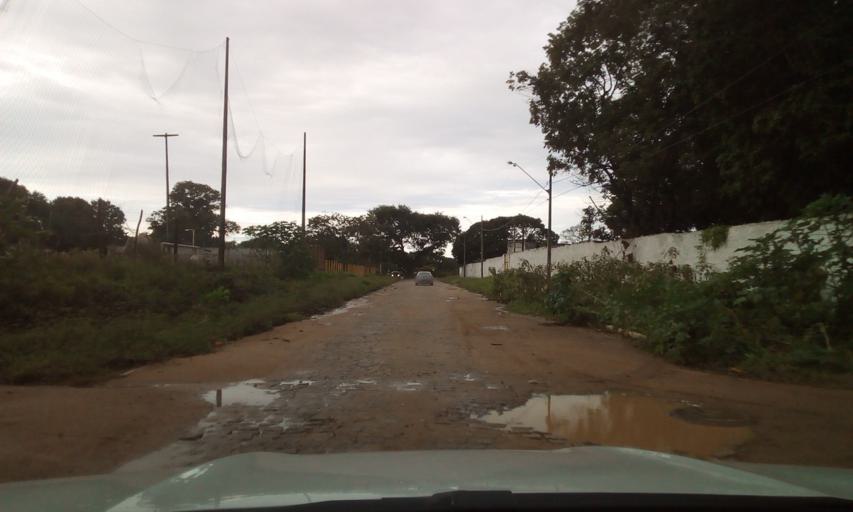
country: BR
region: Paraiba
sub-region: Joao Pessoa
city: Joao Pessoa
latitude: -7.1335
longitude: -34.8255
